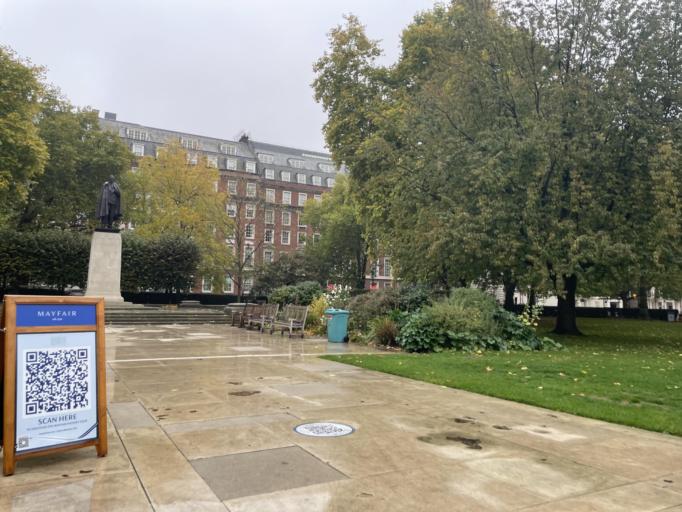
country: GB
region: England
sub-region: Greater London
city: London
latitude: 51.5116
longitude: -0.1514
